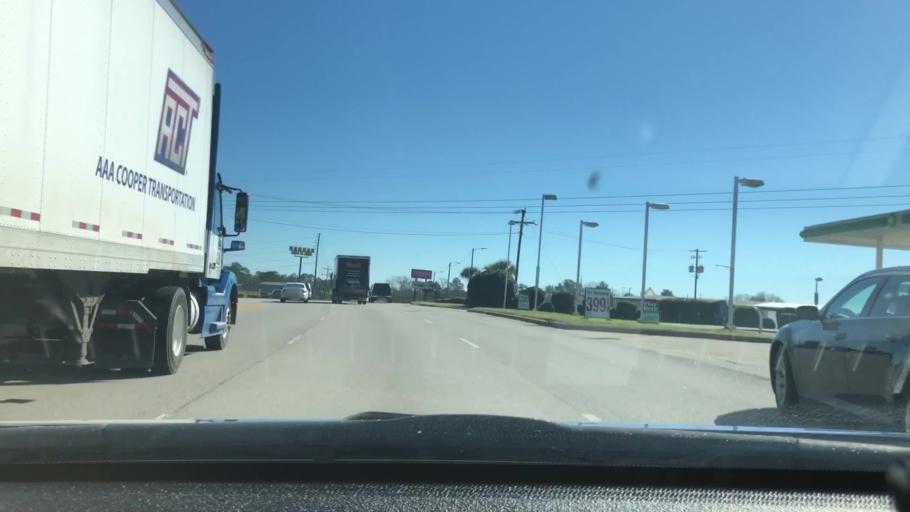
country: US
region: South Carolina
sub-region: Lexington County
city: Oak Grove
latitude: 34.0087
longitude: -81.1460
